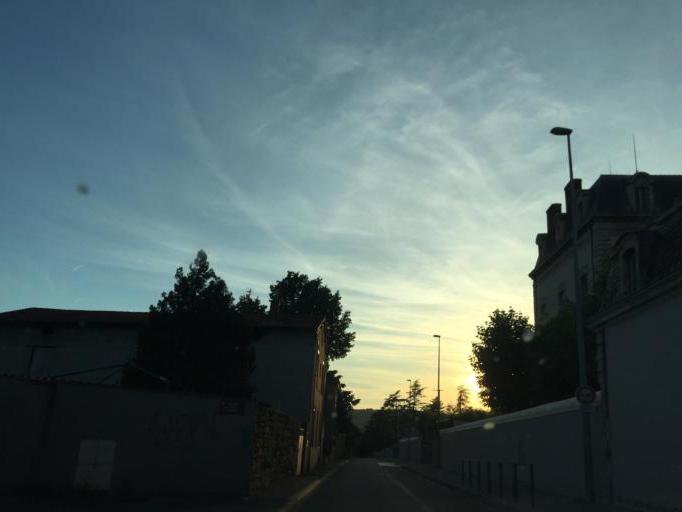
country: FR
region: Rhone-Alpes
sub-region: Departement de la Loire
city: Saint-Chamond
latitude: 45.4711
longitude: 4.5225
